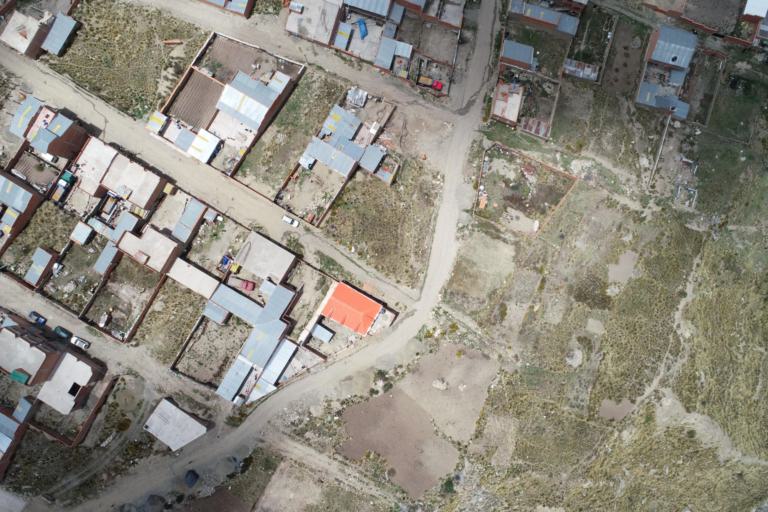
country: BO
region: La Paz
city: La Paz
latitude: -16.4396
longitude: -68.1447
